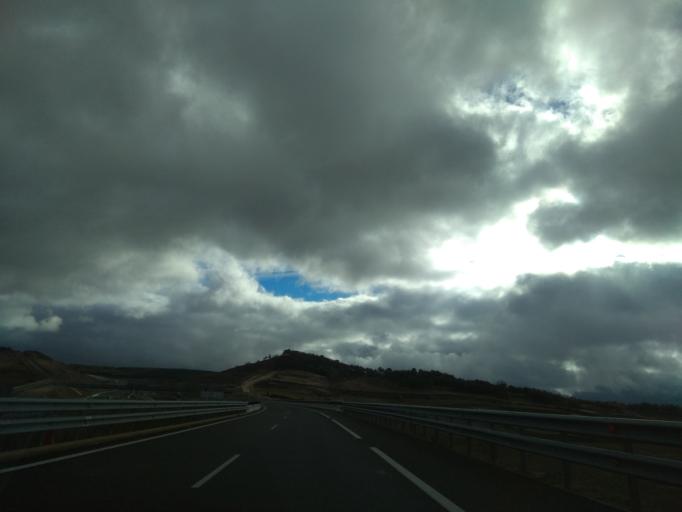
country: ES
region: Castille and Leon
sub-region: Provincia de Burgos
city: Sotragero
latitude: 42.3872
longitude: -3.6908
